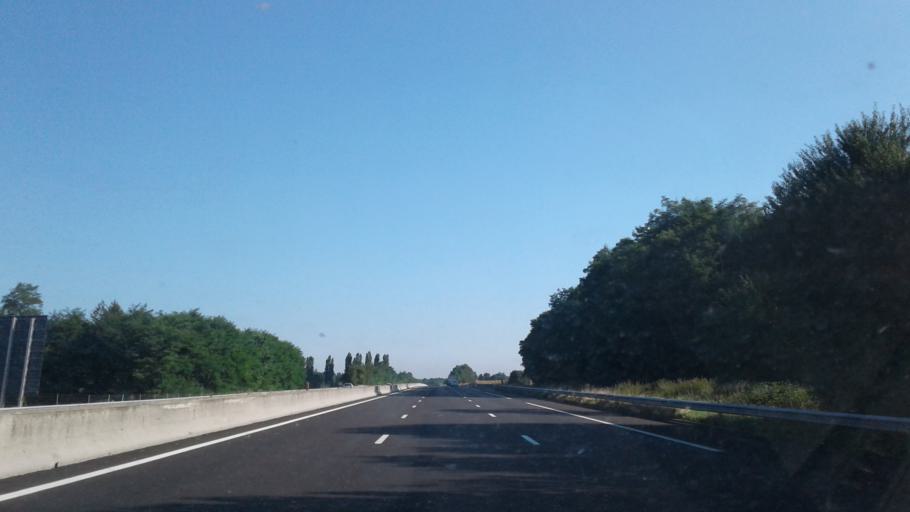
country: FR
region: Rhone-Alpes
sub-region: Departement de l'Ain
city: Saint-Martin-du-Mont
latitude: 46.0955
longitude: 5.2893
